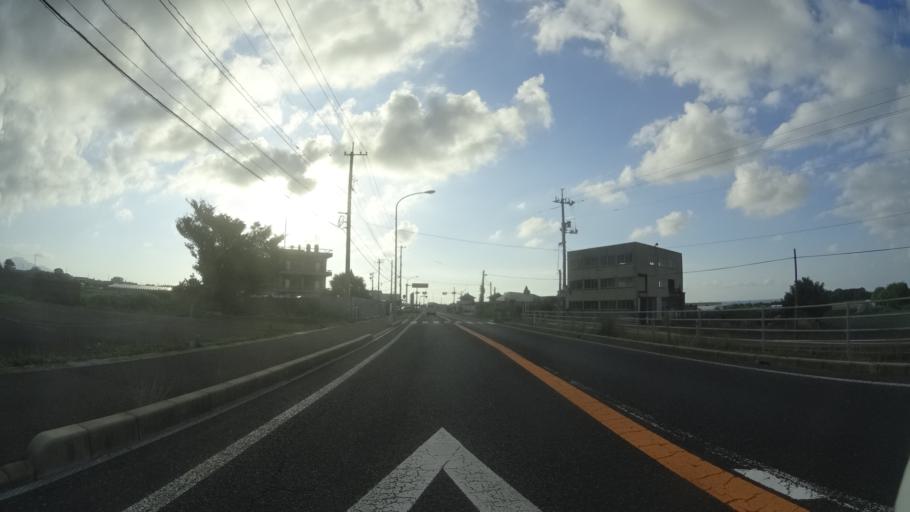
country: JP
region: Tottori
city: Kurayoshi
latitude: 35.5244
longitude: 133.5861
